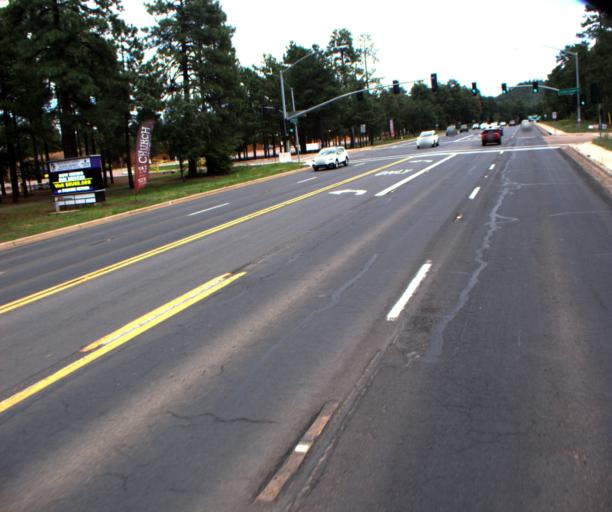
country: US
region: Arizona
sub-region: Navajo County
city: Pinetop-Lakeside
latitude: 34.1475
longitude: -109.9671
